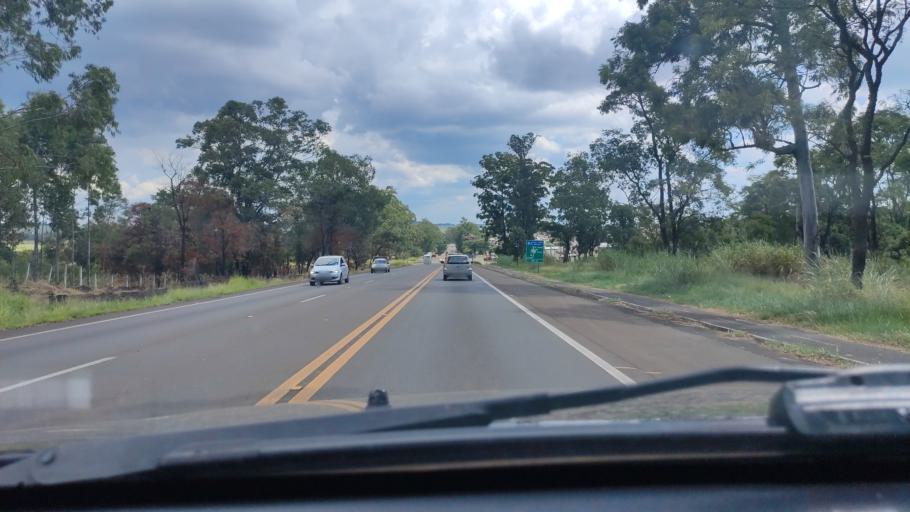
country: BR
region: Sao Paulo
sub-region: Sao Carlos
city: Sao Carlos
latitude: -22.0635
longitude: -47.8859
